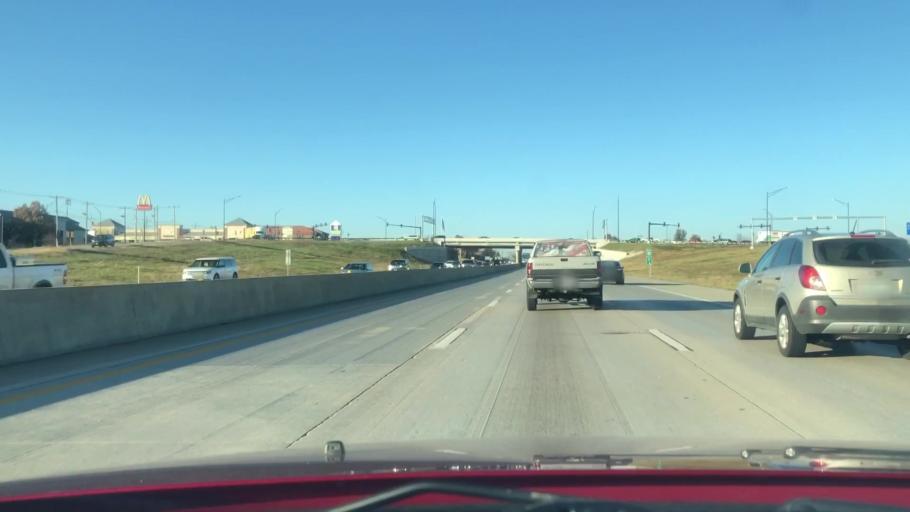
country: US
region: Missouri
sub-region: Greene County
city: Springfield
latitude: 37.1557
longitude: -93.2244
